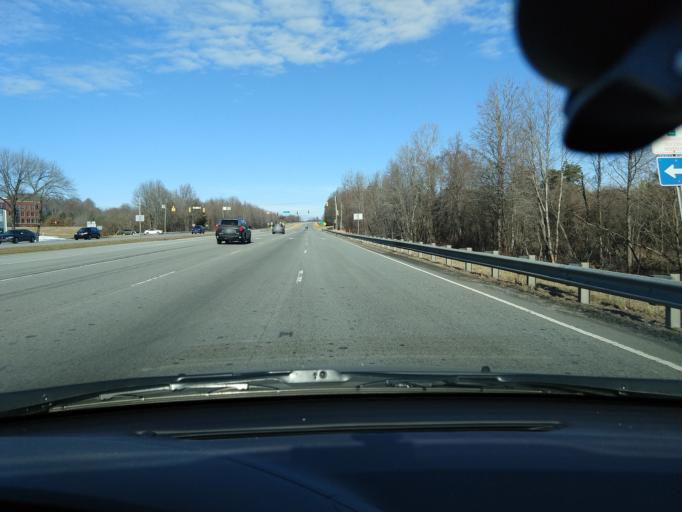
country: US
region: North Carolina
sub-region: Guilford County
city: Oak Ridge
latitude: 36.0851
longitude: -79.9615
